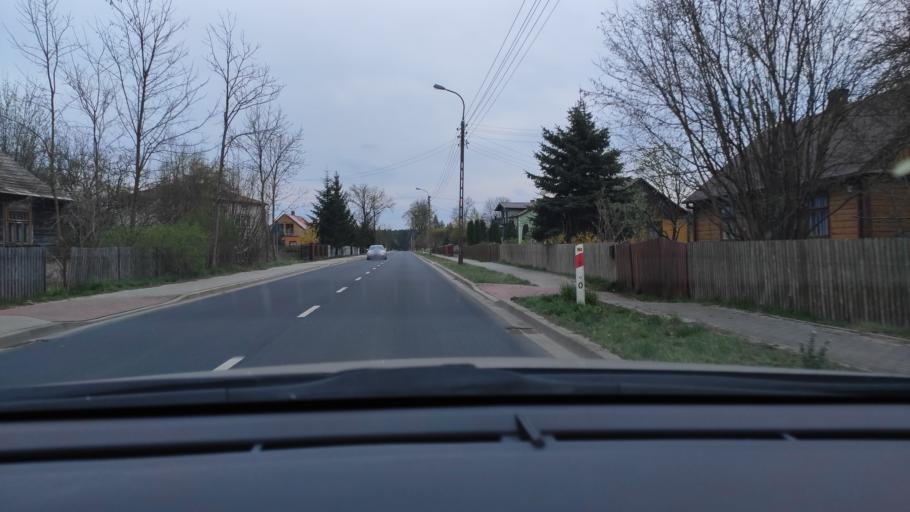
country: PL
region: Masovian Voivodeship
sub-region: Powiat radomski
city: Pionki
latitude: 51.4180
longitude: 21.5104
